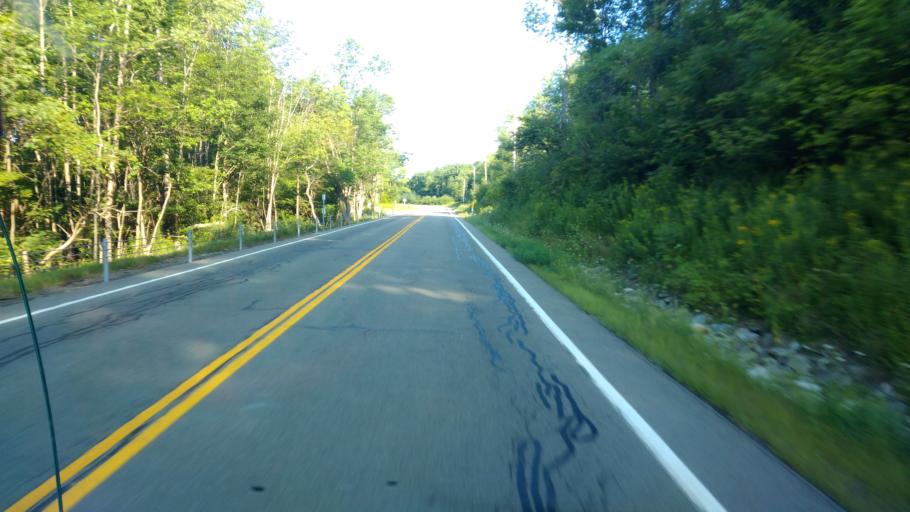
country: US
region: New York
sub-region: Allegany County
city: Andover
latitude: 42.1529
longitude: -77.6964
